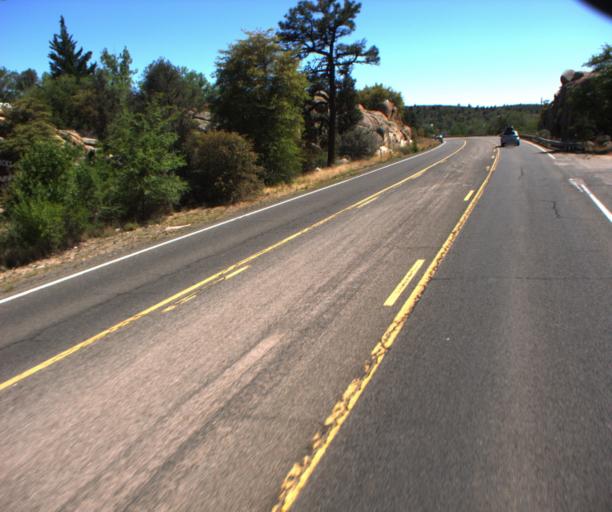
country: US
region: Arizona
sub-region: Yavapai County
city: Prescott
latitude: 34.5972
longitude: -112.4258
